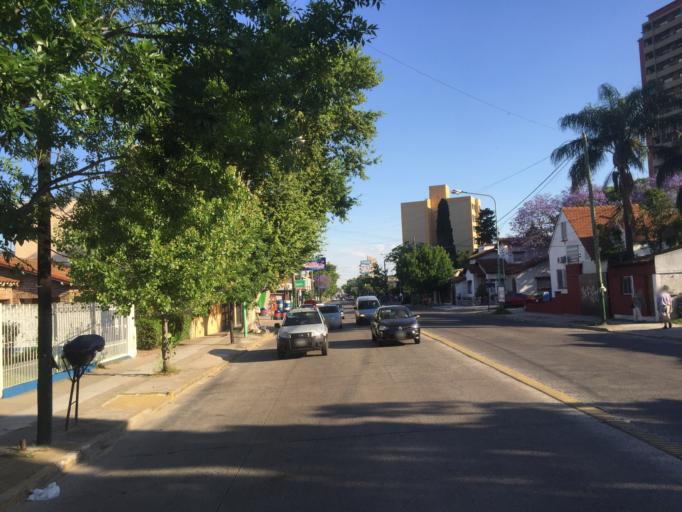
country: AR
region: Buenos Aires
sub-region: Partido de Lomas de Zamora
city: Lomas de Zamora
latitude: -34.7707
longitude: -58.3961
